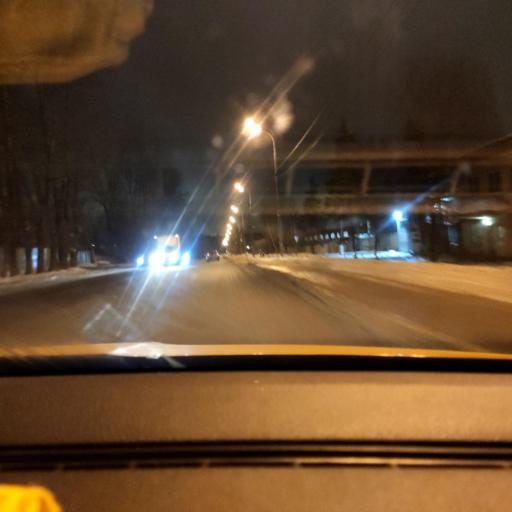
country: RU
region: Moskovskaya
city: Odintsovo
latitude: 55.6599
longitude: 37.2860
